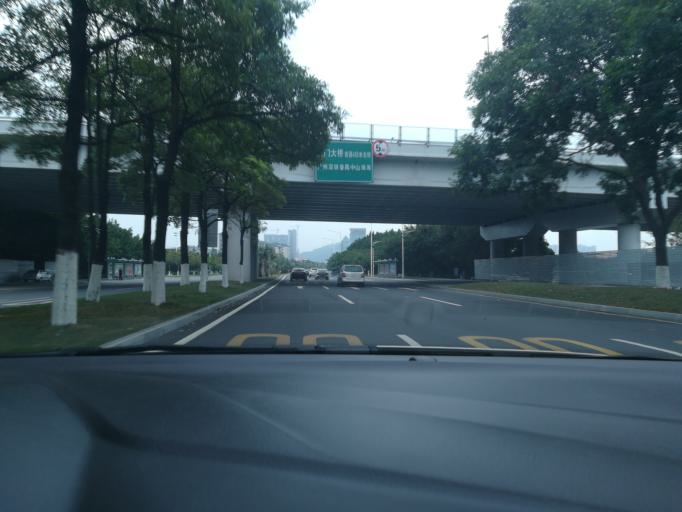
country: CN
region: Guangdong
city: Nansha
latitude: 22.7819
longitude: 113.5930
